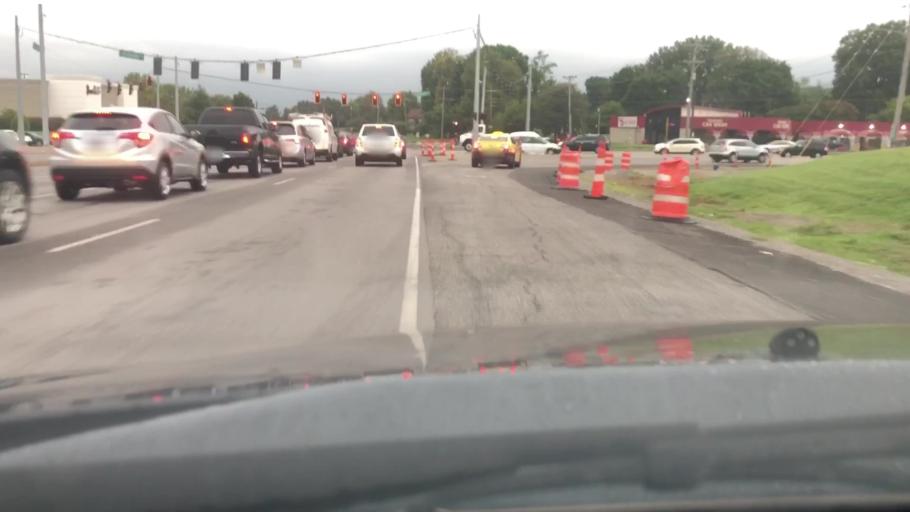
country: US
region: Kentucky
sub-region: Jefferson County
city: Hurstbourne Acres
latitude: 38.2152
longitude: -85.5902
